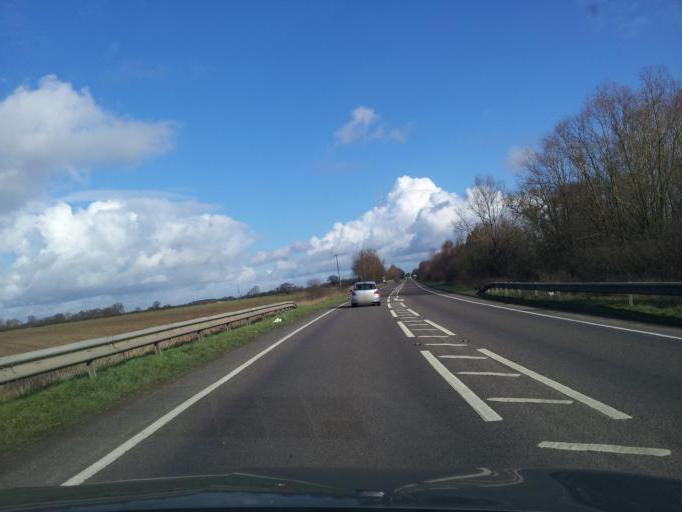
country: GB
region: England
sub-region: Norfolk
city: Diss
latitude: 52.4001
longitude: 1.1803
